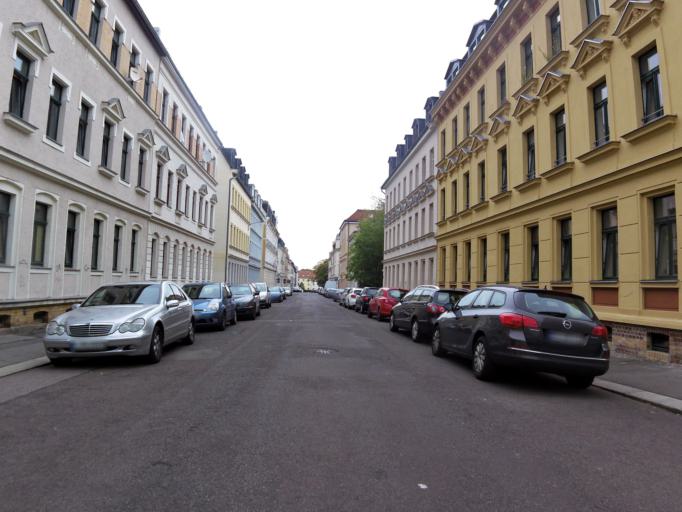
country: DE
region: Saxony
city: Leipzig
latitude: 51.3399
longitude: 12.3240
